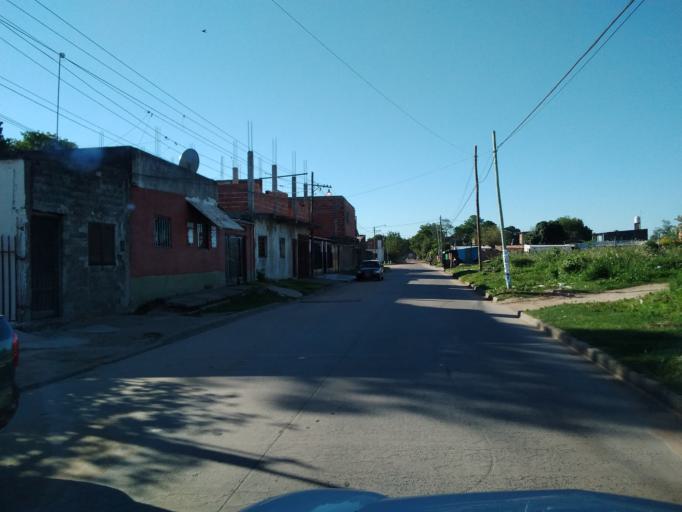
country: AR
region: Corrientes
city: Corrientes
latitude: -27.4717
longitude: -58.7962
